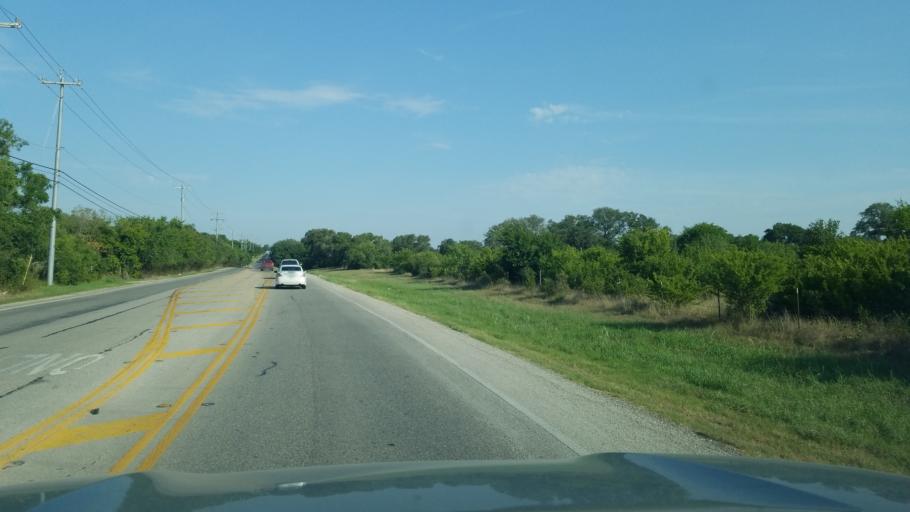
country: US
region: Texas
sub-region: Bexar County
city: Helotes
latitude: 29.4617
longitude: -98.7588
